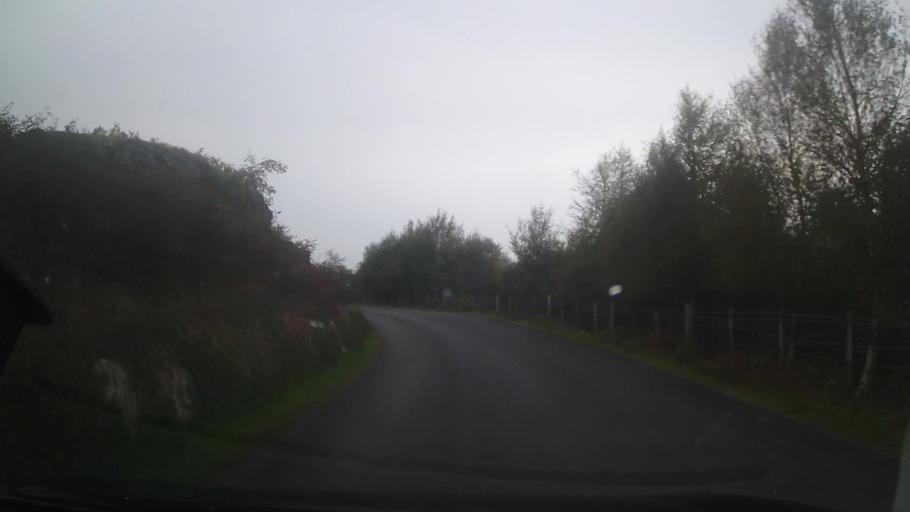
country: GB
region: Wales
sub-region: Sir Powys
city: Rhayader
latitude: 52.3049
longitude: -3.6276
